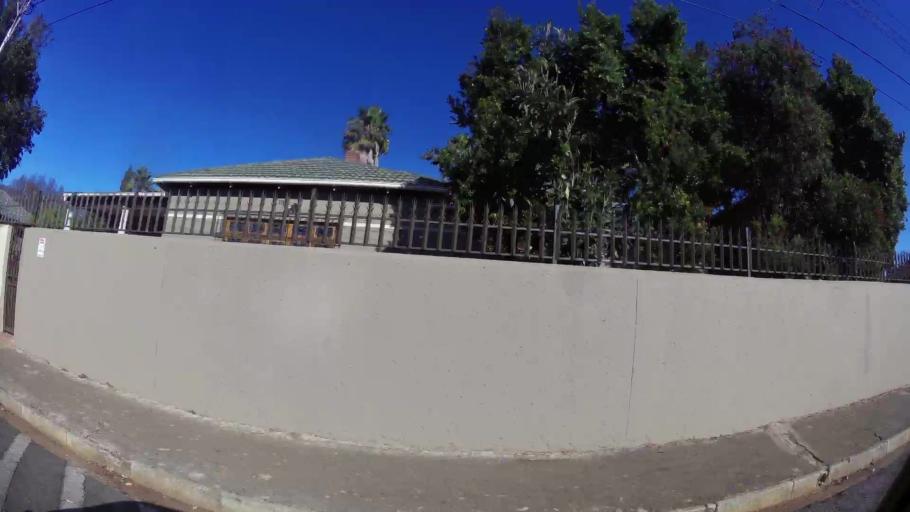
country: ZA
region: Gauteng
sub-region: City of Johannesburg Metropolitan Municipality
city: Johannesburg
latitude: -26.1872
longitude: 28.1116
